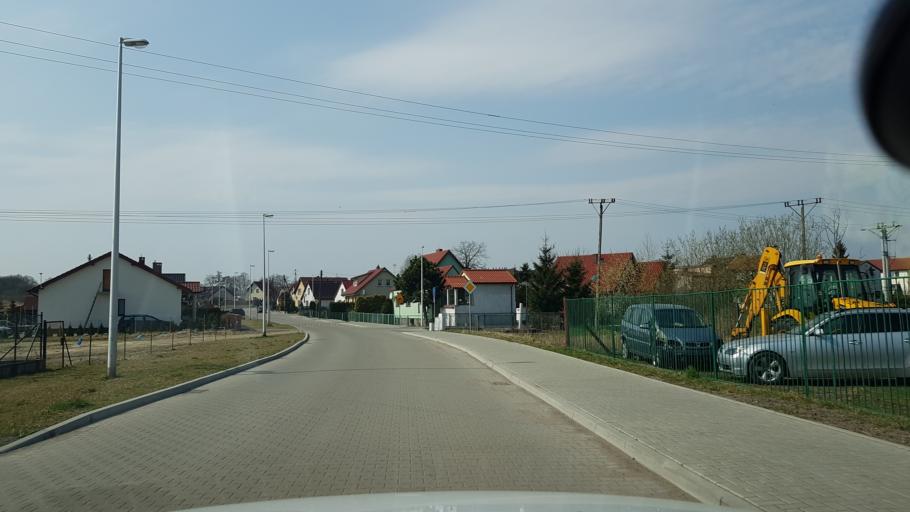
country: PL
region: West Pomeranian Voivodeship
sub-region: Powiat stargardzki
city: Stargard Szczecinski
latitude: 53.3445
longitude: 15.0712
